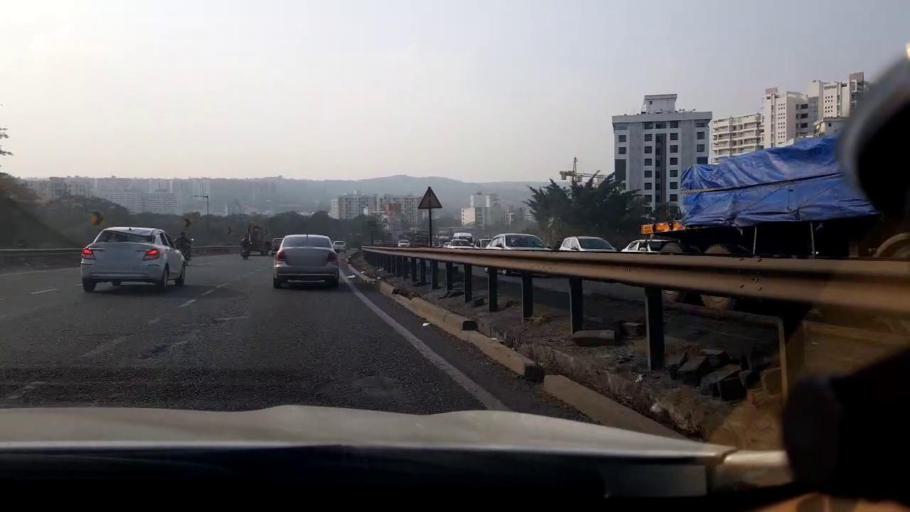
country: IN
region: Maharashtra
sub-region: Pune Division
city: Kharakvasla
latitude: 18.5091
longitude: 73.7754
